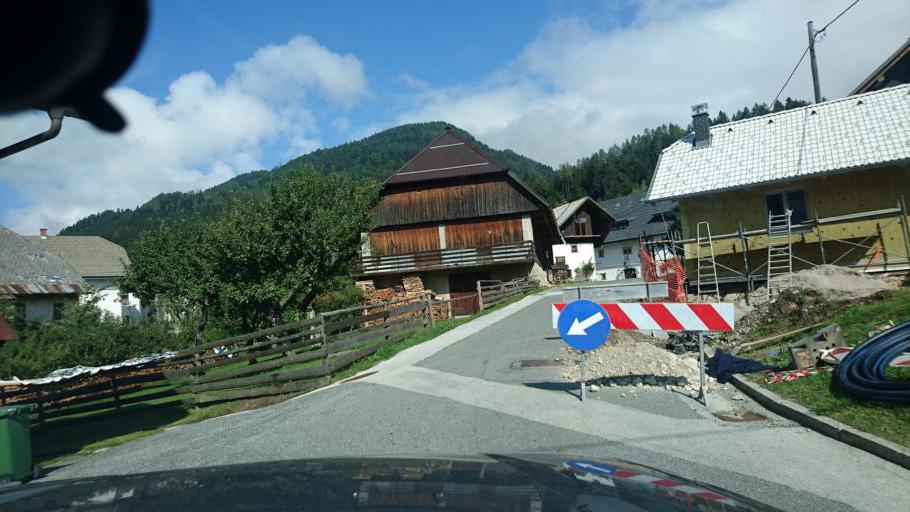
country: SI
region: Kranjska Gora
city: Kranjska Gora
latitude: 46.4933
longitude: 13.7575
